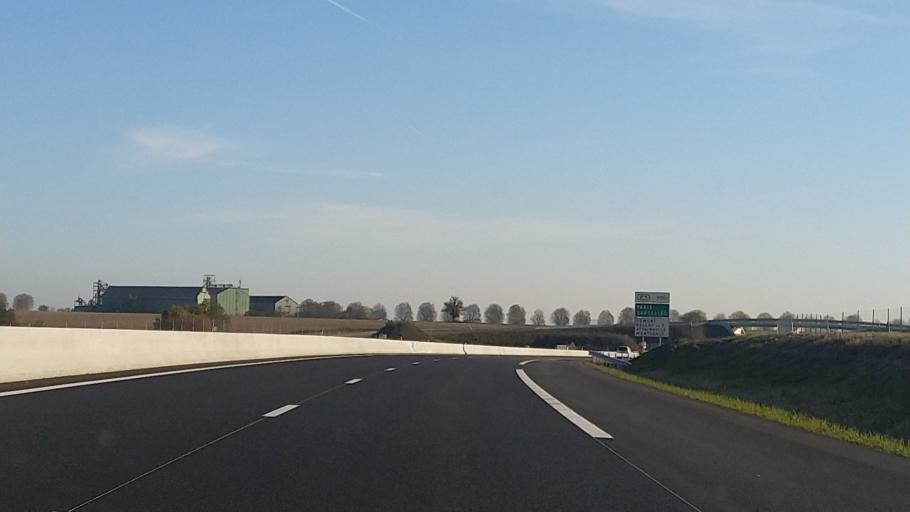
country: FR
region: Ile-de-France
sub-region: Departement du Val-d'Oise
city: Montsoult
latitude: 49.0807
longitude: 2.3291
